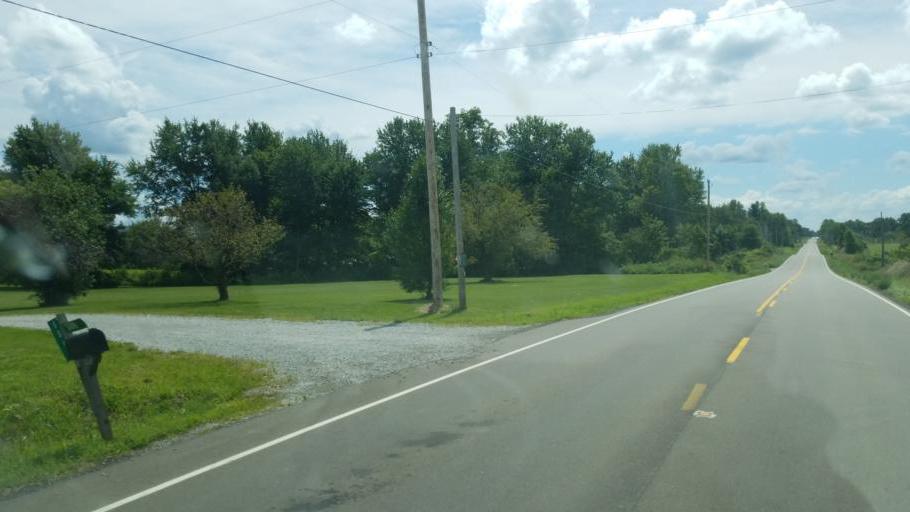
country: US
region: Ohio
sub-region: Knox County
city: Centerburg
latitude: 40.3225
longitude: -82.6697
